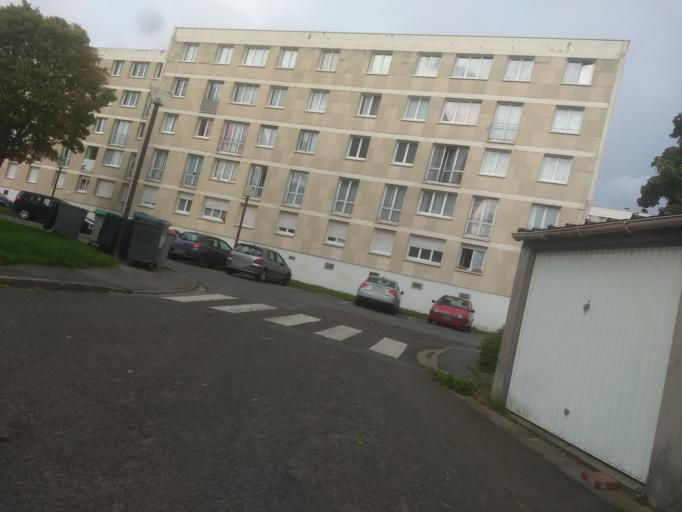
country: FR
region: Nord-Pas-de-Calais
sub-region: Departement du Pas-de-Calais
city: Achicourt
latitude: 50.2911
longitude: 2.7502
